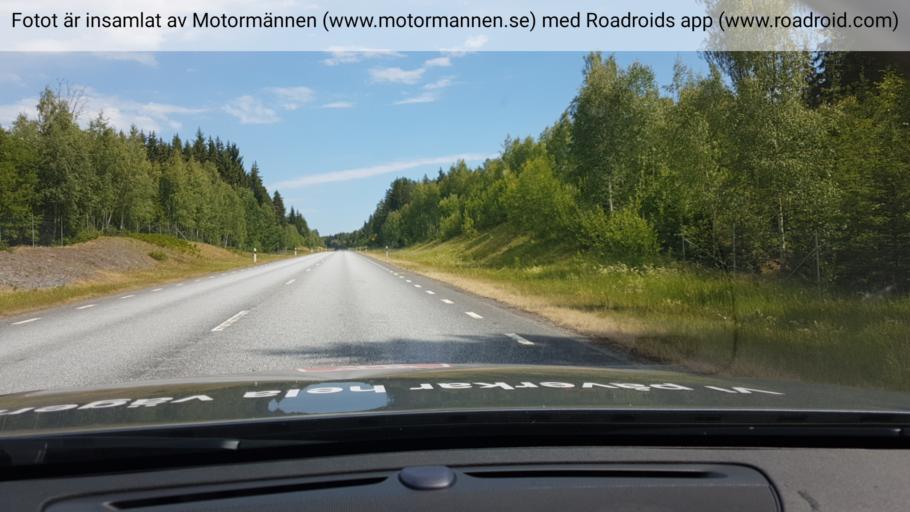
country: SE
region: Uppsala
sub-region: Osthammars Kommun
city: Gimo
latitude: 60.1659
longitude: 18.2178
